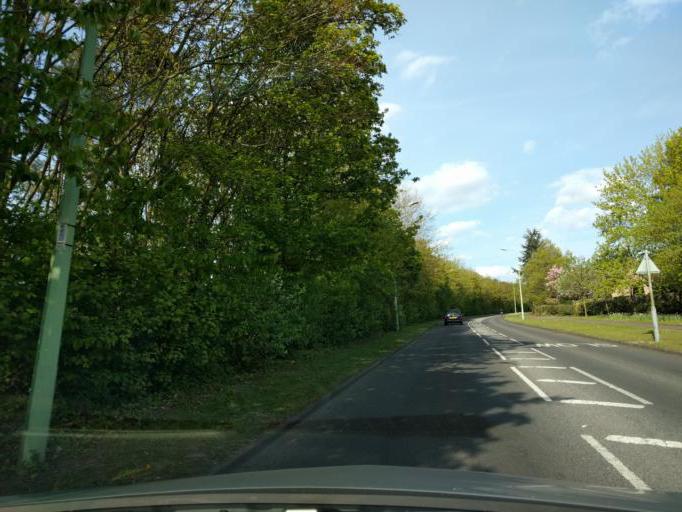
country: GB
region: England
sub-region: Suffolk
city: Bury St Edmunds
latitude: 52.2427
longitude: 0.7299
